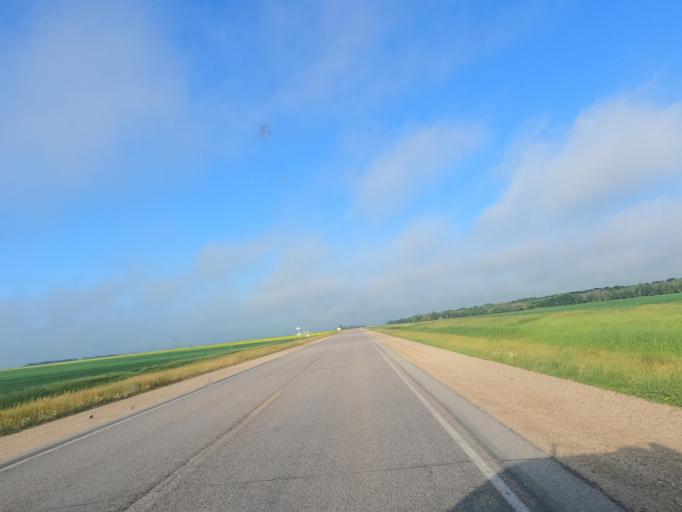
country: CA
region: Manitoba
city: Headingley
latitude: 49.7661
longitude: -97.6265
